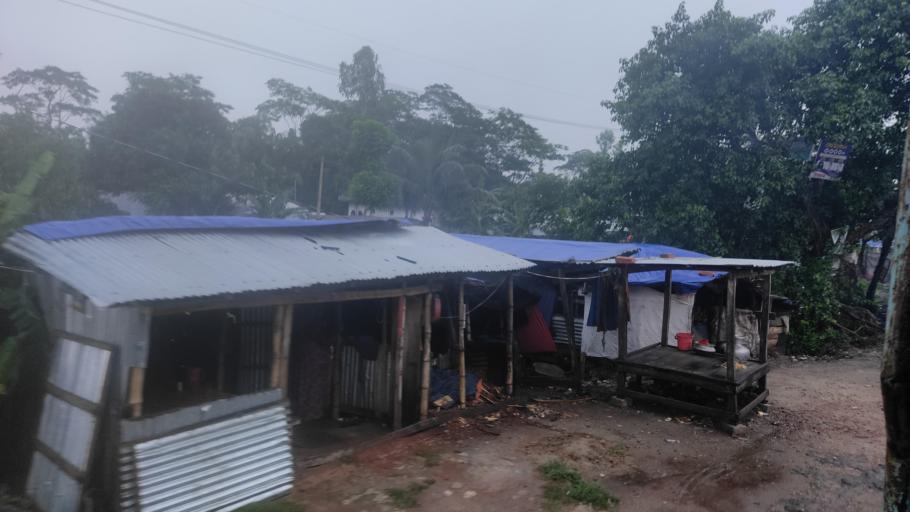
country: BD
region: Barisal
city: Bhandaria
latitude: 22.2940
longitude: 90.3252
